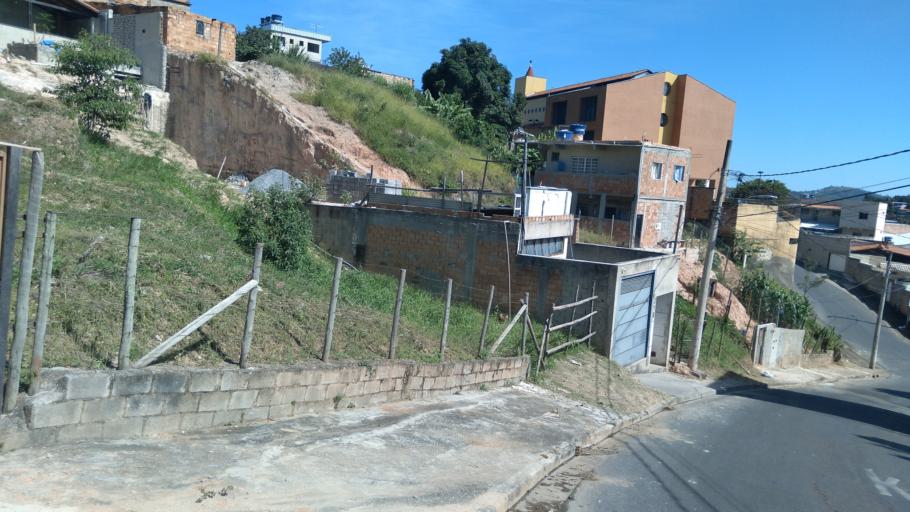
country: BR
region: Minas Gerais
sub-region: Belo Horizonte
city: Belo Horizonte
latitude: -19.8461
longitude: -43.9047
